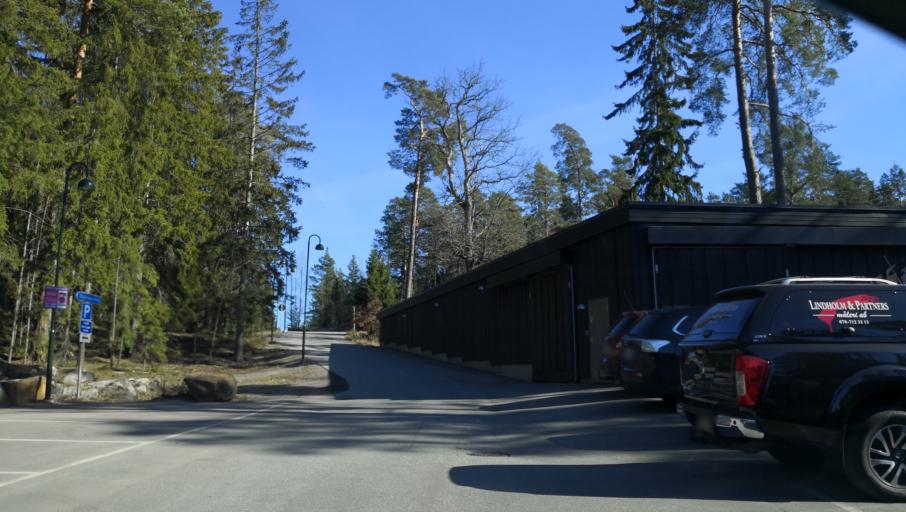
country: SE
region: Stockholm
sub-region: Varmdo Kommun
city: Gustavsberg
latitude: 59.3070
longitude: 18.3486
